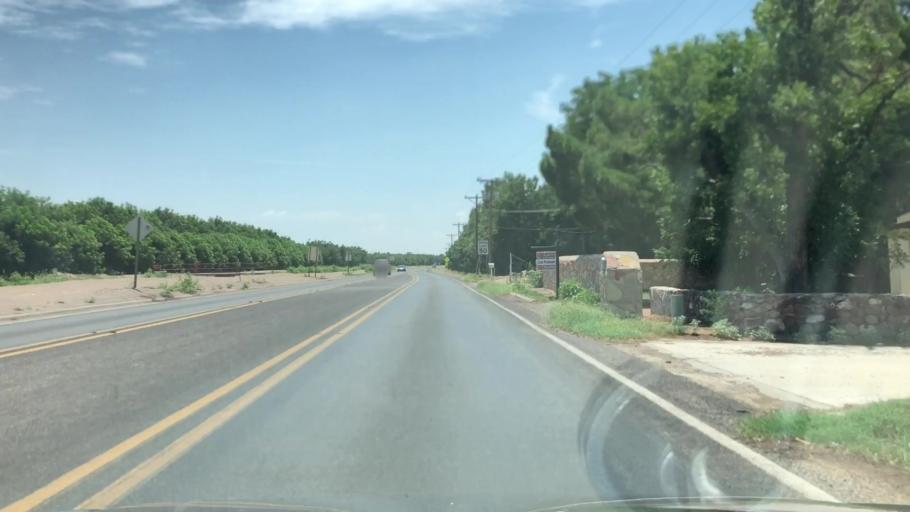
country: US
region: New Mexico
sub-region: Dona Ana County
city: La Union
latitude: 31.9964
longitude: -106.6547
